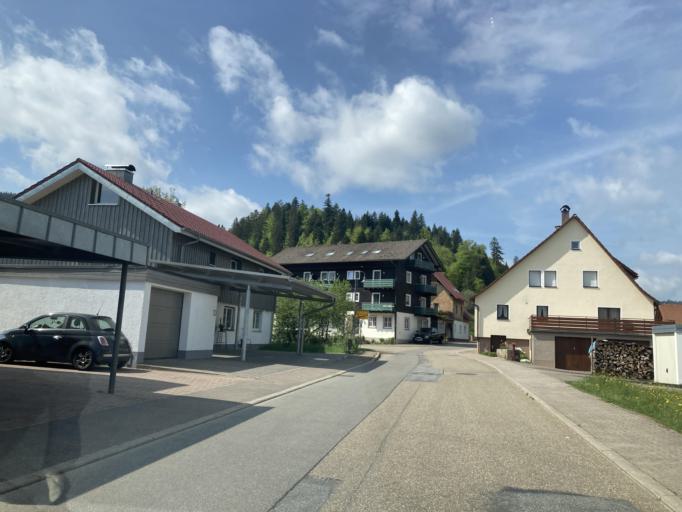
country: DE
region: Baden-Wuerttemberg
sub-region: Karlsruhe Region
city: Biberach
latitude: 48.5278
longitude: 8.2754
